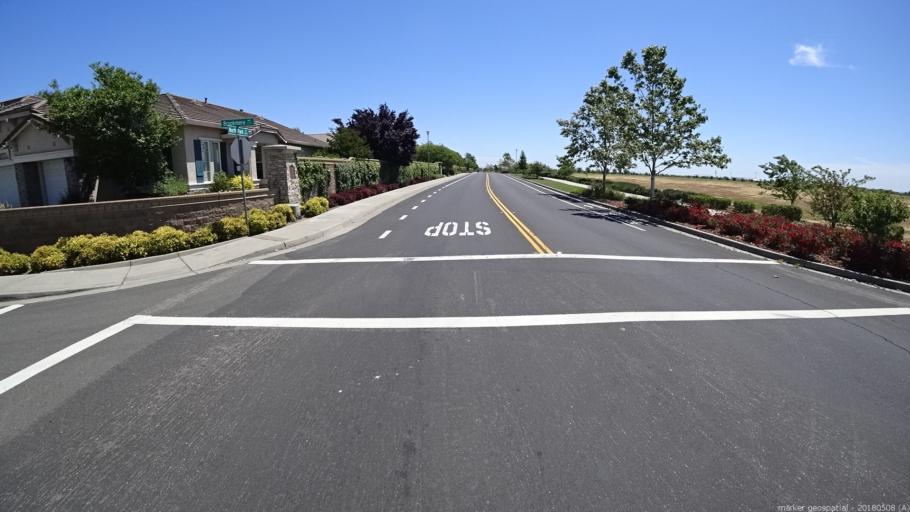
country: US
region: California
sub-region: Sacramento County
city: Elverta
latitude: 38.6665
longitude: -121.5240
